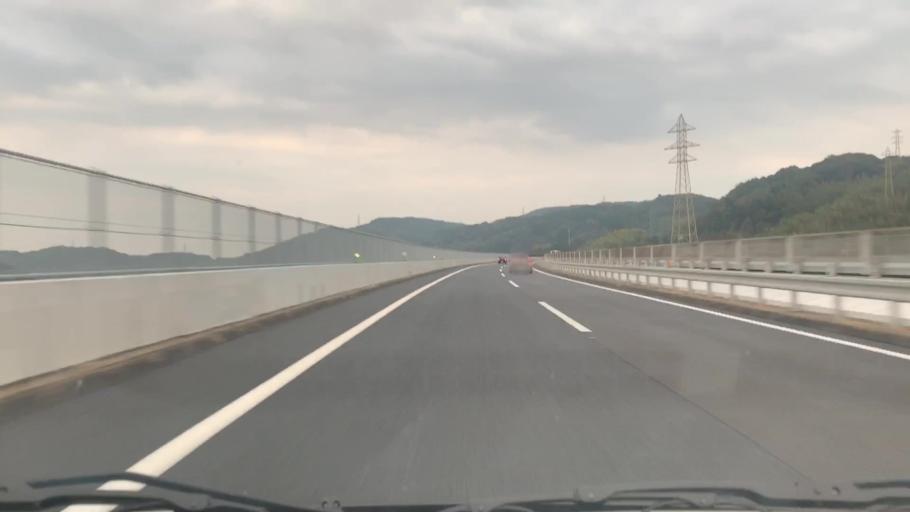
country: JP
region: Nagasaki
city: Omura
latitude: 32.8898
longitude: 129.9903
